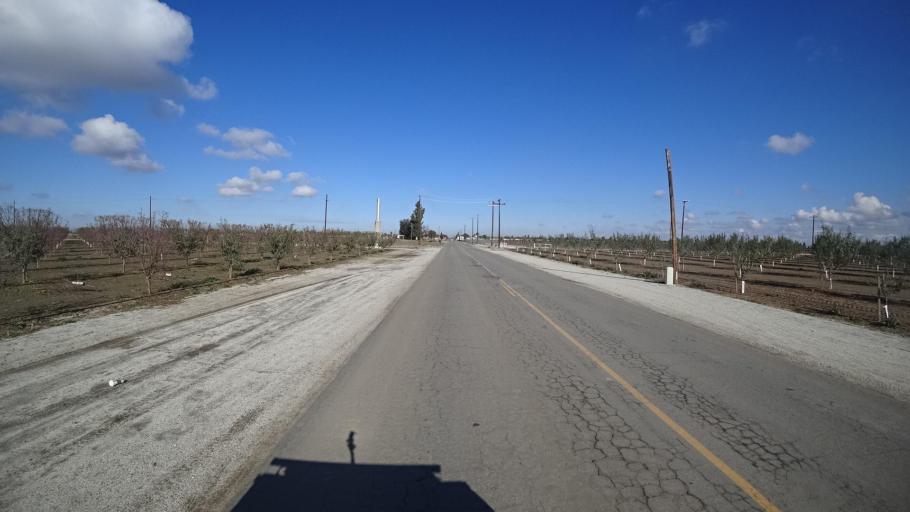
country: US
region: California
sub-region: Kern County
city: McFarland
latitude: 35.6595
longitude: -119.2323
